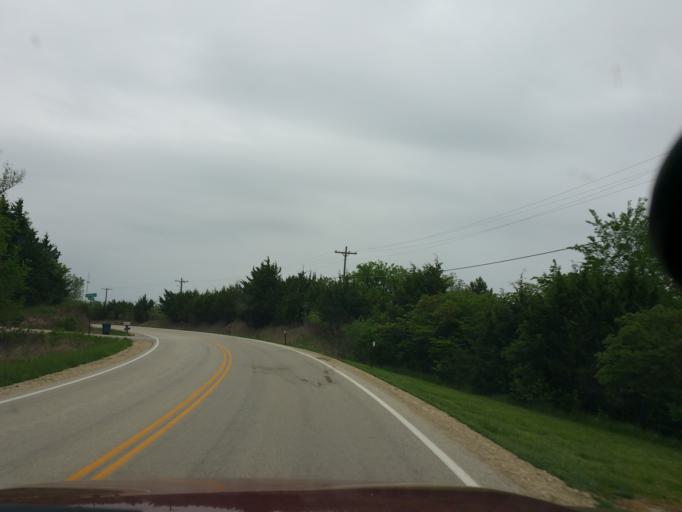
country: US
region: Kansas
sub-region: Riley County
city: Manhattan
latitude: 39.2585
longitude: -96.6173
